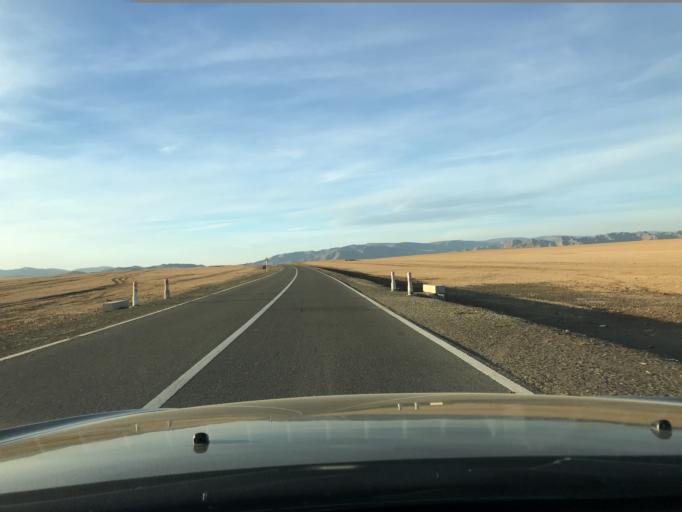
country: MN
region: Central Aimak
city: Arhust
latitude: 47.7562
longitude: 107.4462
